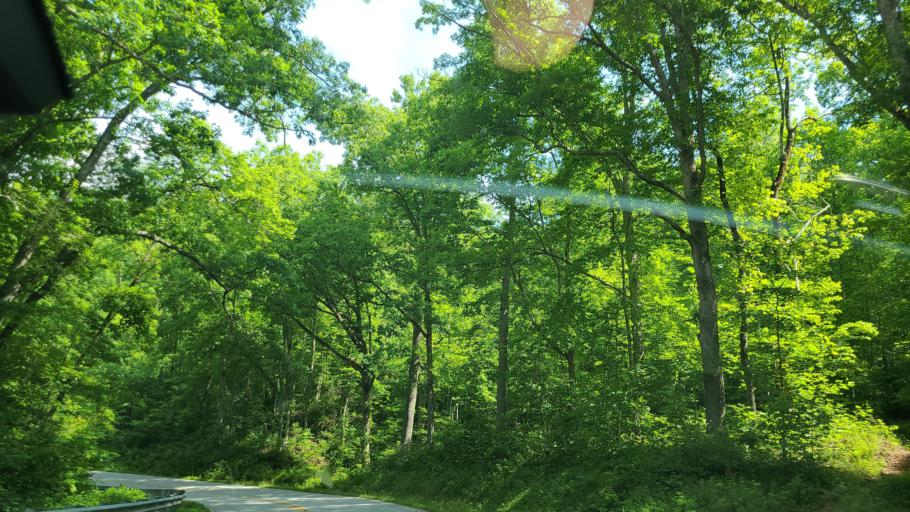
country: US
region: South Carolina
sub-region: Oconee County
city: Walhalla
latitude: 34.8975
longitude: -83.1739
